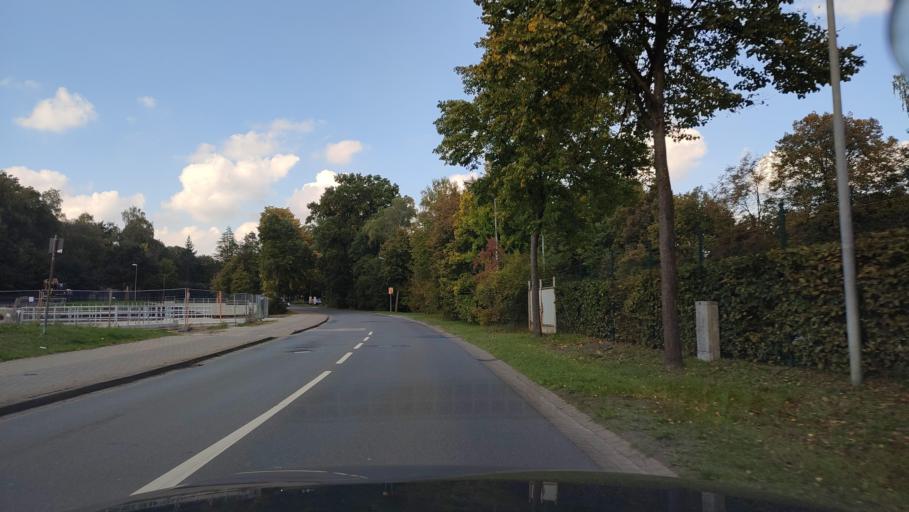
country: DE
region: Lower Saxony
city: Bomlitz
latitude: 52.9059
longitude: 9.6563
